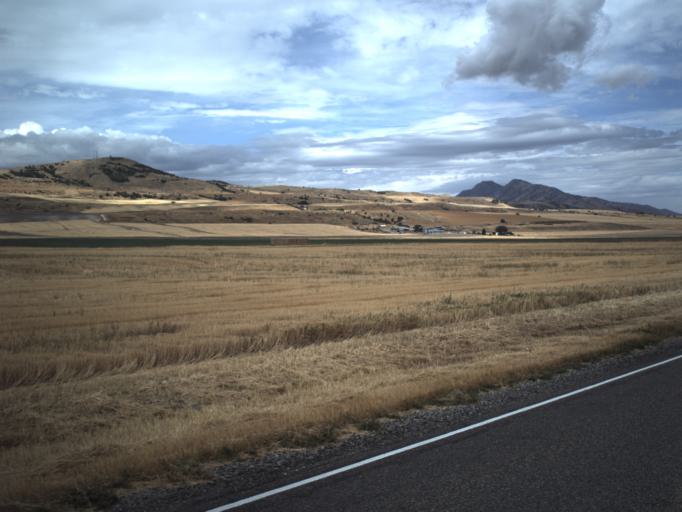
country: US
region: Utah
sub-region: Cache County
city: Benson
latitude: 41.8130
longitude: -111.9959
